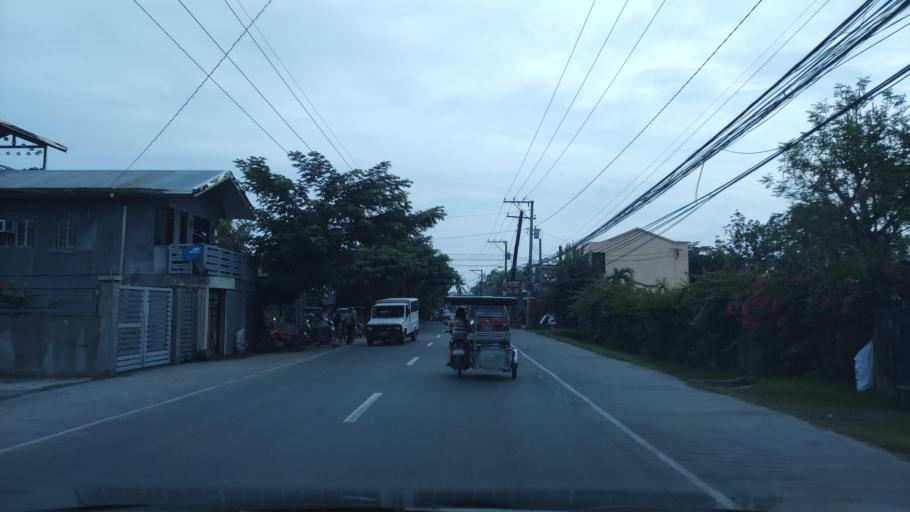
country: PH
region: Central Luzon
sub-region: Province of Pampanga
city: Santa Ana
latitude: 15.1011
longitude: 120.7698
